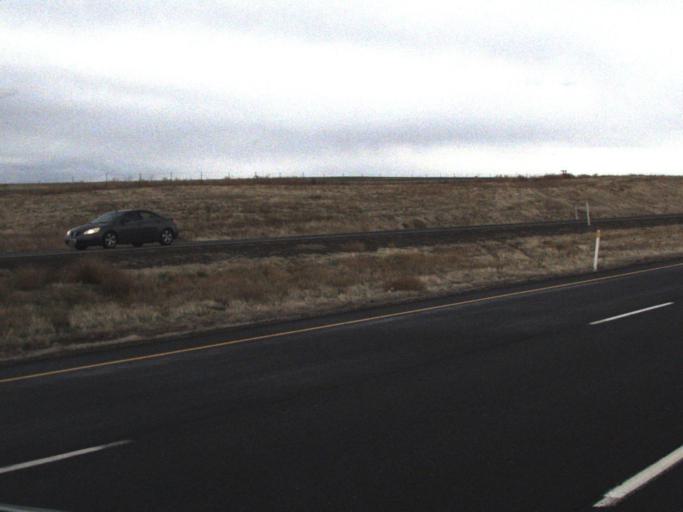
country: US
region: Washington
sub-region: Walla Walla County
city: Garrett
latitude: 46.0486
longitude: -118.4867
